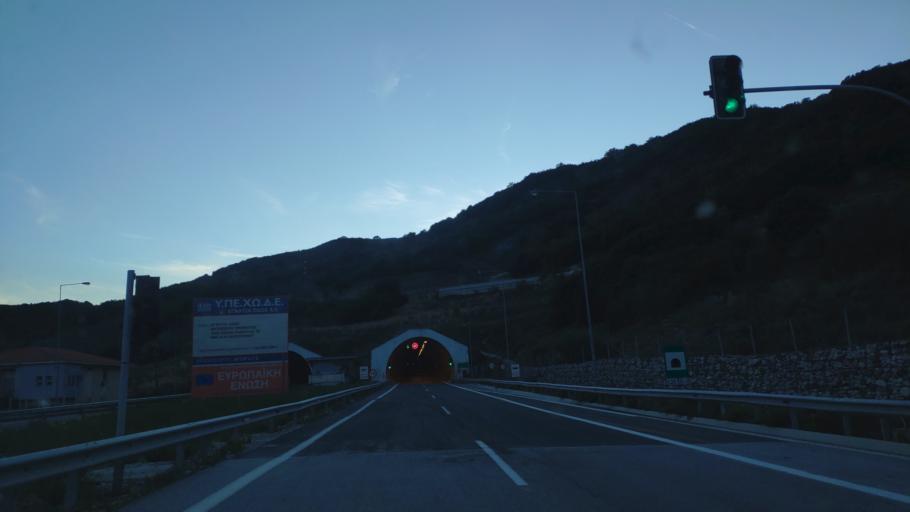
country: GR
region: Epirus
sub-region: Nomos Ioanninon
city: Metsovo
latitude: 39.7342
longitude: 21.0475
